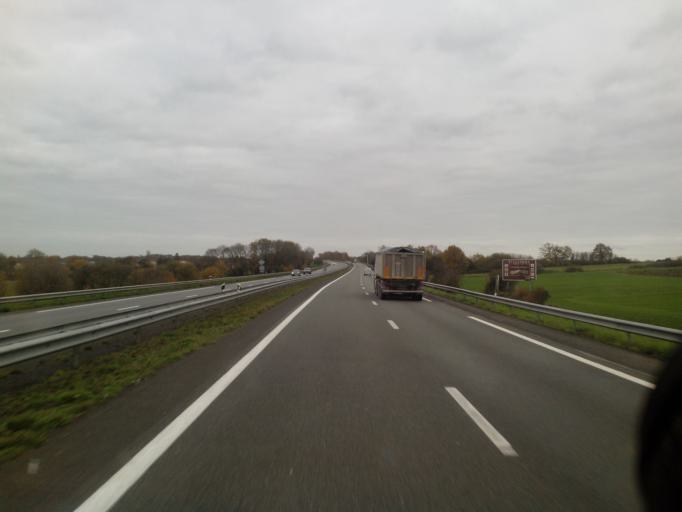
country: FR
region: Pays de la Loire
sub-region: Departement de Maine-et-Loire
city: Tillieres
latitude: 47.1419
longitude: -1.1747
